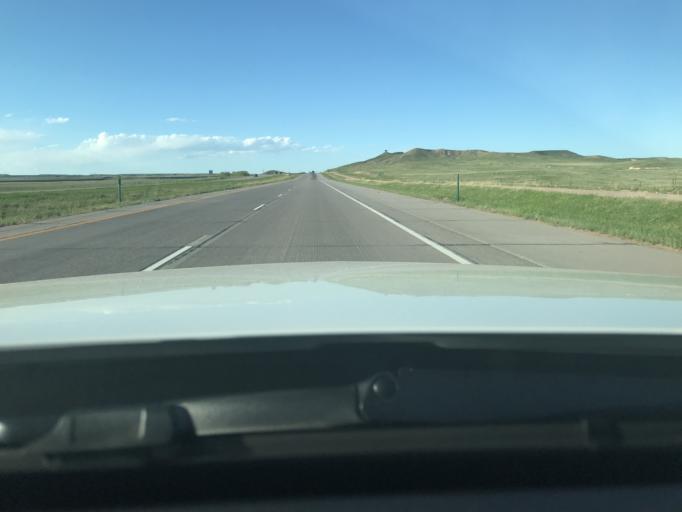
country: US
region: Wyoming
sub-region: Laramie County
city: South Greeley
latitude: 40.9637
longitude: -104.9224
